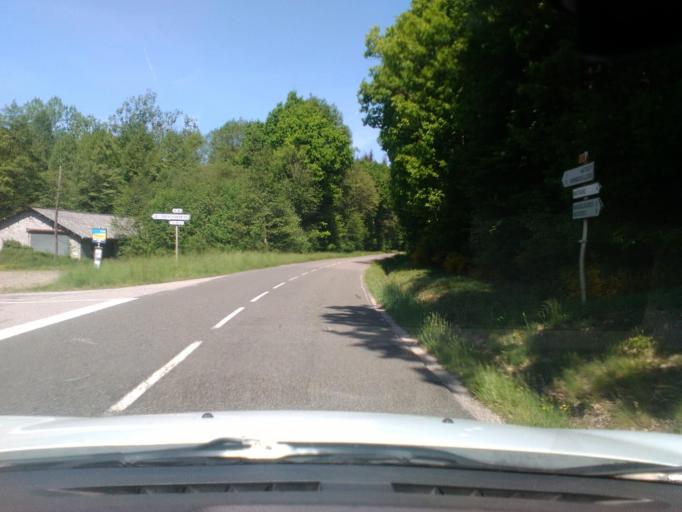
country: FR
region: Lorraine
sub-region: Departement des Vosges
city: Jeanmenil
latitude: 48.2747
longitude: 6.7143
